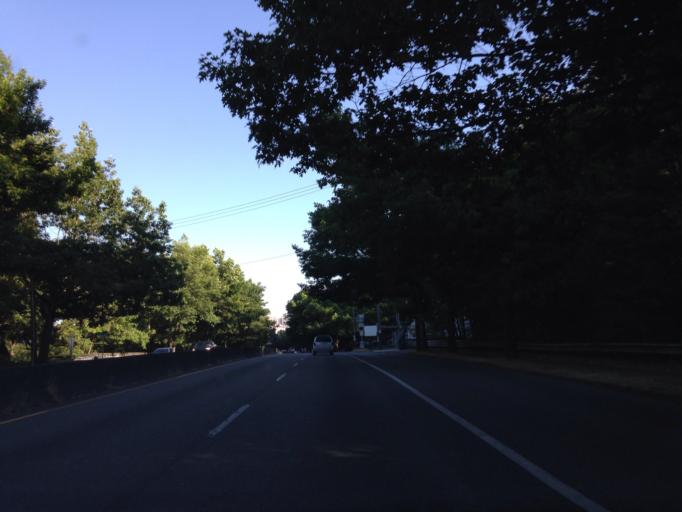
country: US
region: Washington
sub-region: King County
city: Seattle
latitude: 47.6397
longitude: -122.3460
